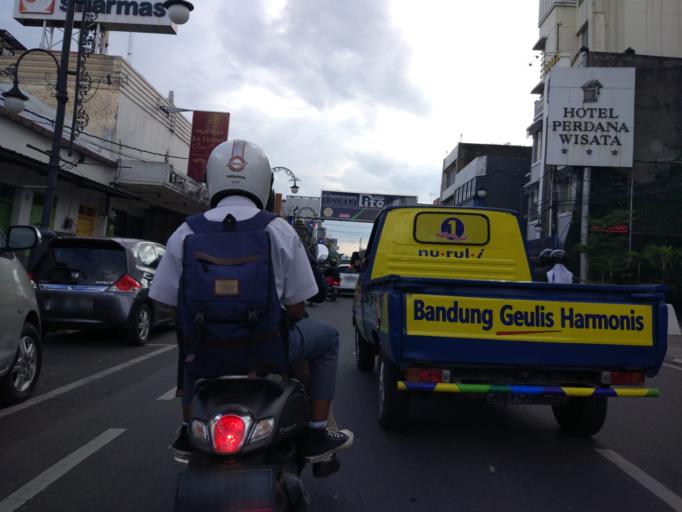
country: ID
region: West Java
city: Bandung
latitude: -6.9205
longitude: 107.6017
